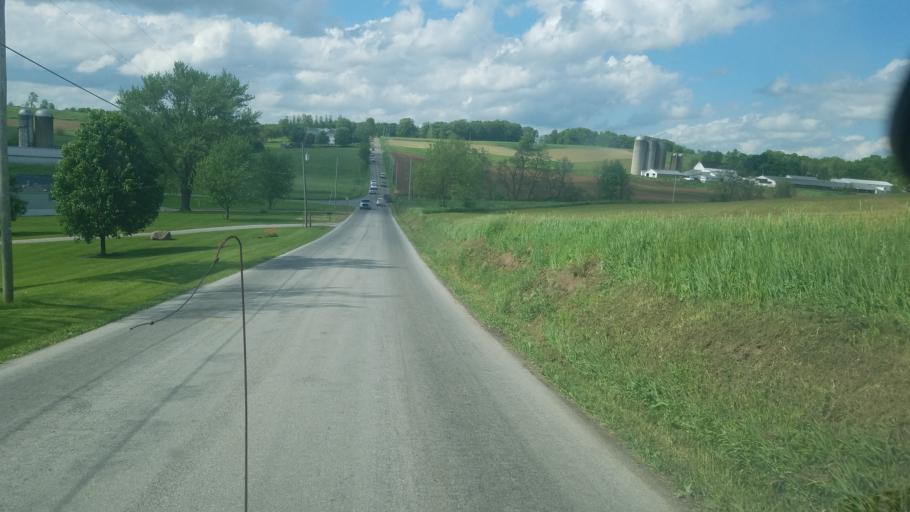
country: US
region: Ohio
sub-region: Wayne County
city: Apple Creek
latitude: 40.6880
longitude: -81.8520
